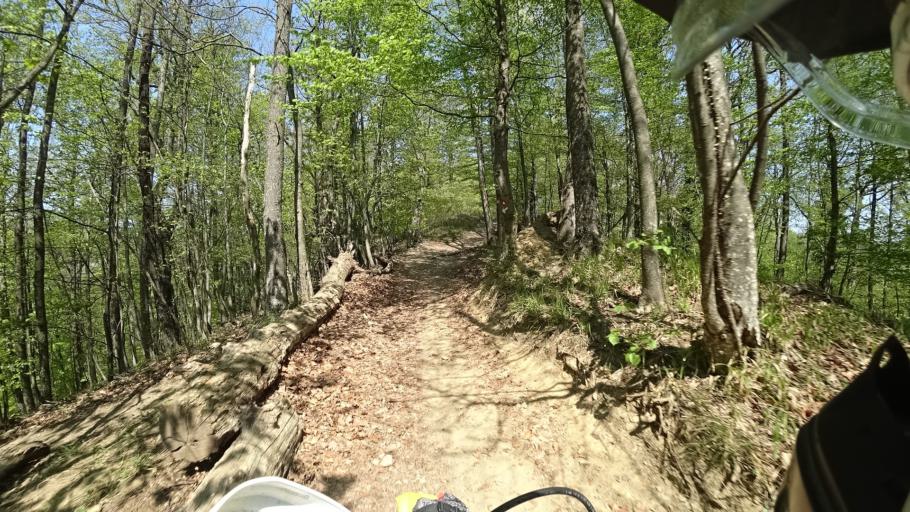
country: HR
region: Zagrebacka
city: Jablanovec
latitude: 45.8700
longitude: 15.9021
